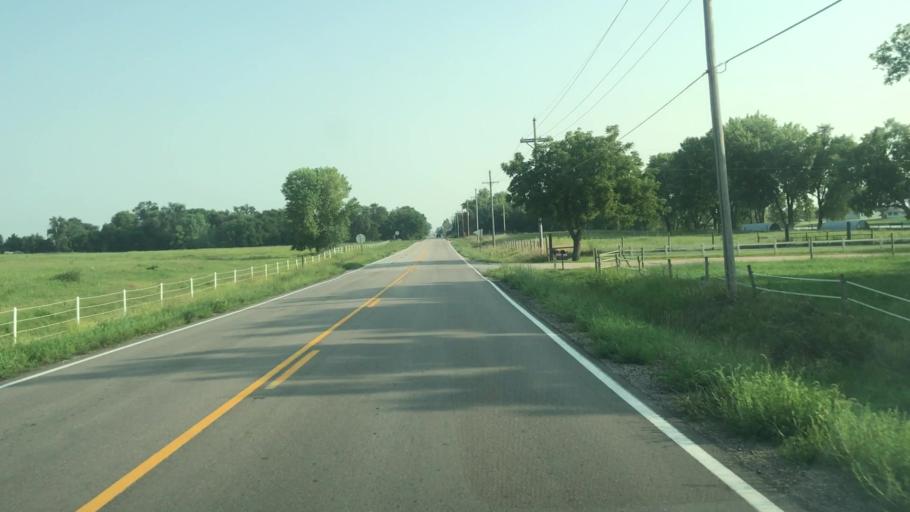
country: US
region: Nebraska
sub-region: Hall County
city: Grand Island
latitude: 40.9132
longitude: -98.3018
